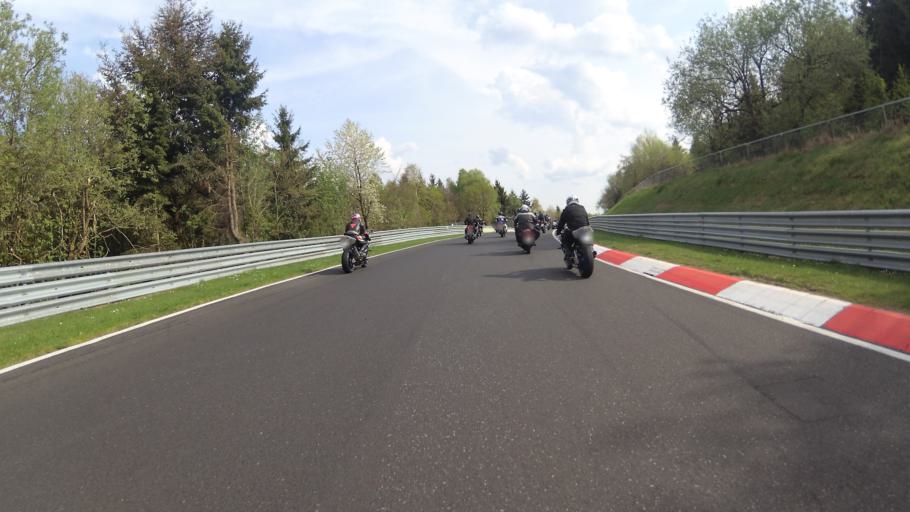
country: DE
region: Rheinland-Pfalz
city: Drees
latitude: 50.3556
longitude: 6.9859
